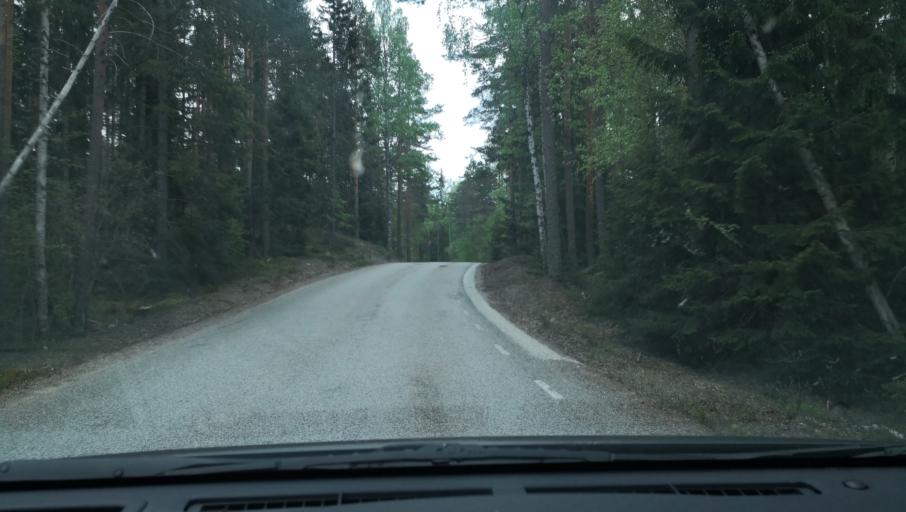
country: SE
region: Vaestmanland
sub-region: Skinnskattebergs Kommun
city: Skinnskatteberg
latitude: 59.8174
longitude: 15.5539
